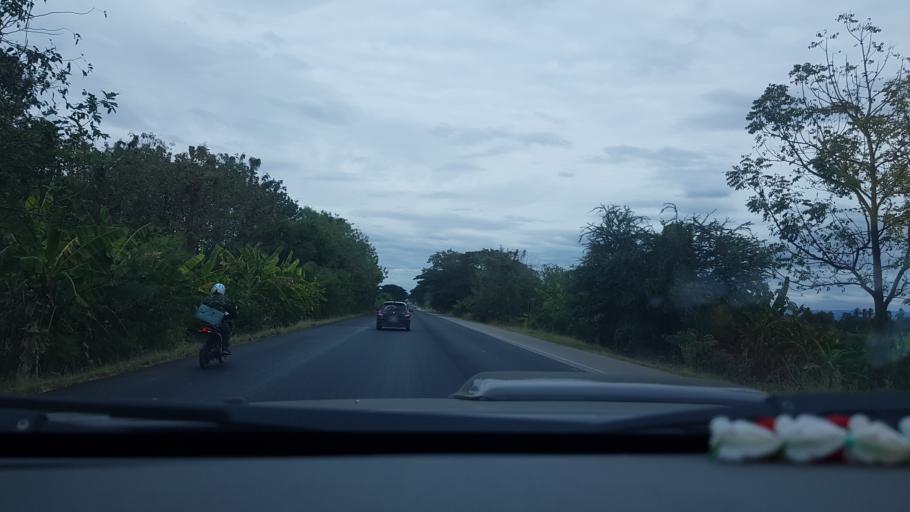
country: TH
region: Phetchabun
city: Phetchabun
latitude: 16.4552
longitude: 101.1167
